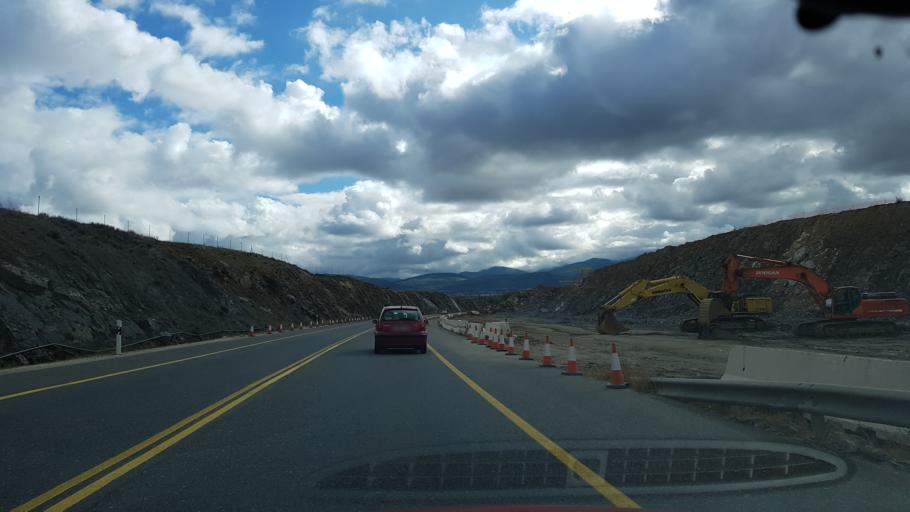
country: ES
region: Castille and Leon
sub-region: Provincia de Segovia
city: San Cristobal de Segovia
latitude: 40.9453
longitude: -4.0866
